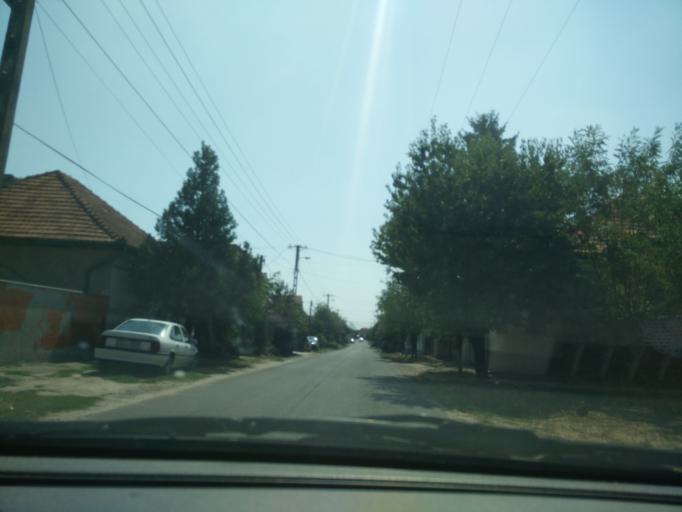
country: HU
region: Heves
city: Hatvan
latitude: 47.6651
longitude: 19.7012
